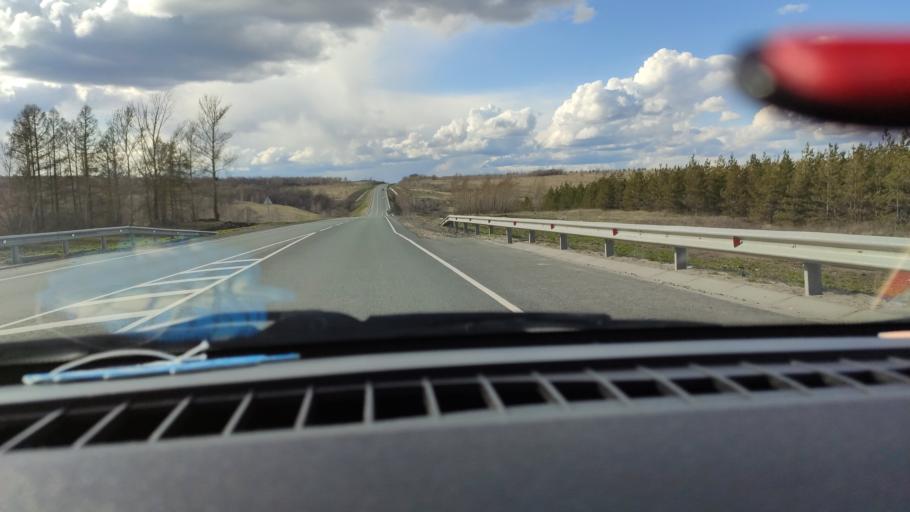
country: RU
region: Saratov
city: Shikhany
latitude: 52.1393
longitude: 47.2112
